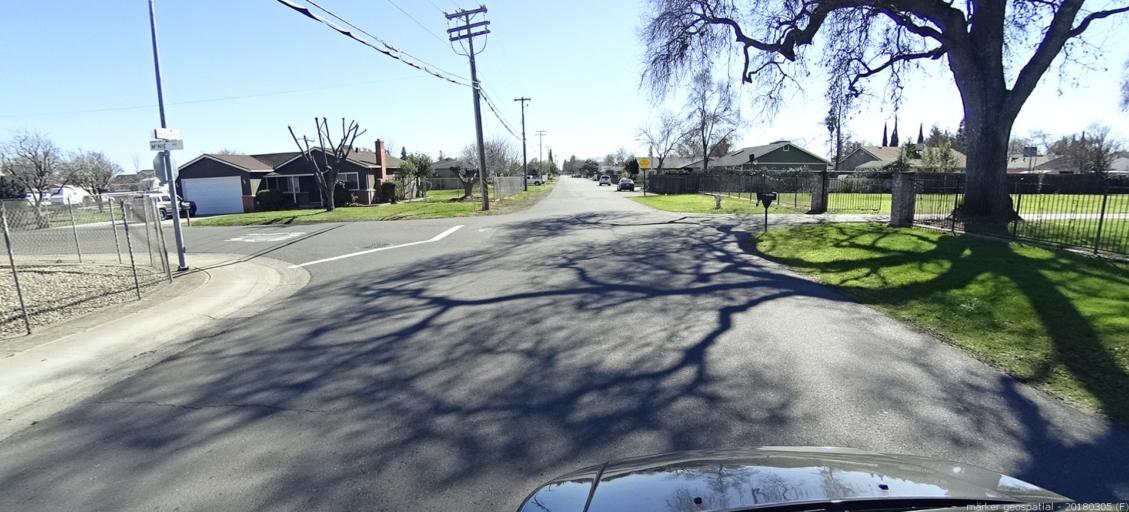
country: US
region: California
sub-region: Sacramento County
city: Florin
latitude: 38.4945
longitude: -121.3997
